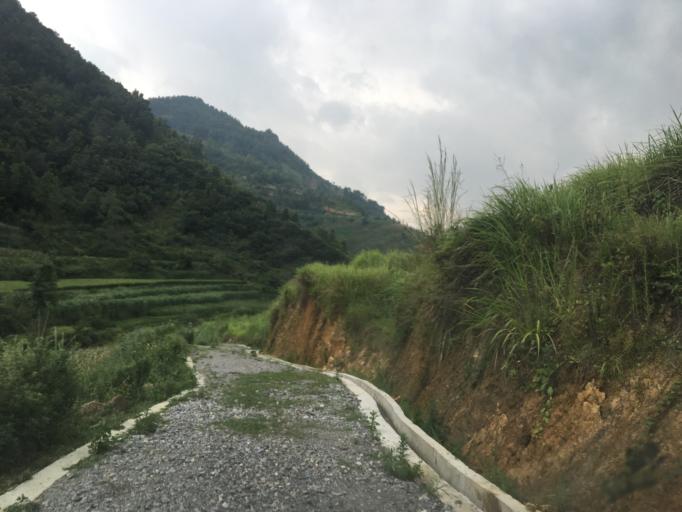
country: CN
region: Guangxi Zhuangzu Zizhiqu
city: Xinzhou
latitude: 25.1703
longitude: 105.6977
